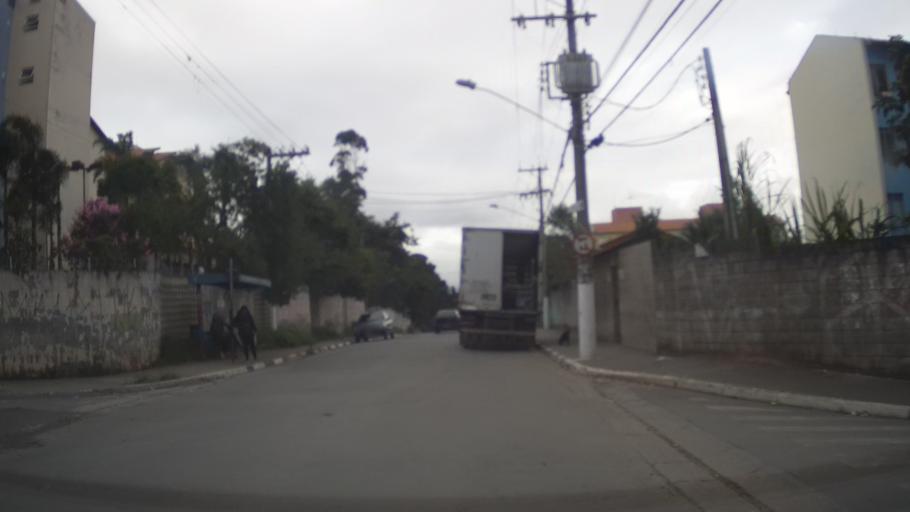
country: BR
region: Sao Paulo
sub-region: Itaquaquecetuba
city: Itaquaquecetuba
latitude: -23.4523
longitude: -46.3992
